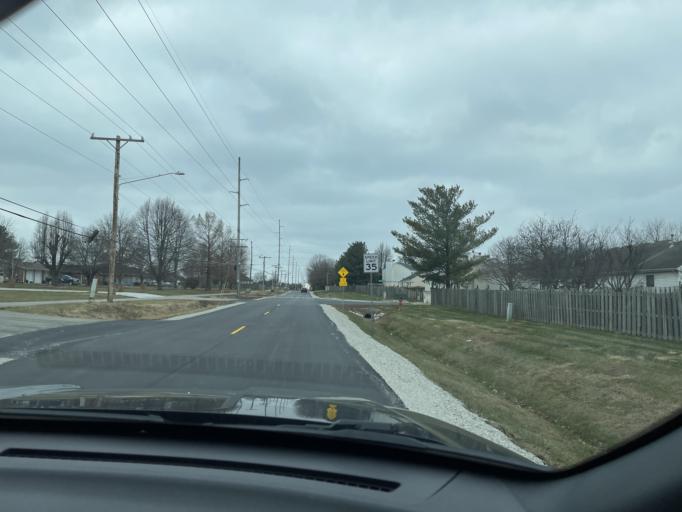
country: US
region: Illinois
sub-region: Sangamon County
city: Rochester
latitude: 39.7673
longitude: -89.5788
